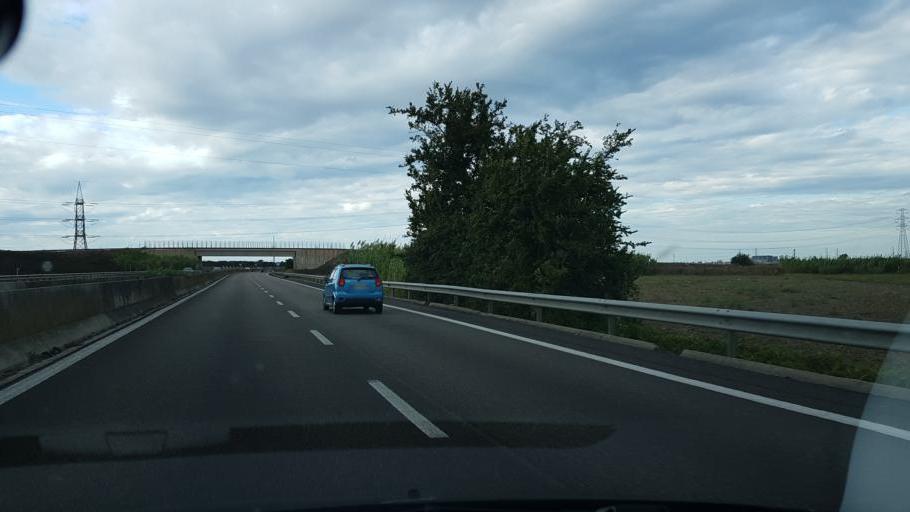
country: IT
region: Apulia
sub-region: Provincia di Brindisi
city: La Rosa
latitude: 40.5973
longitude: 17.9683
